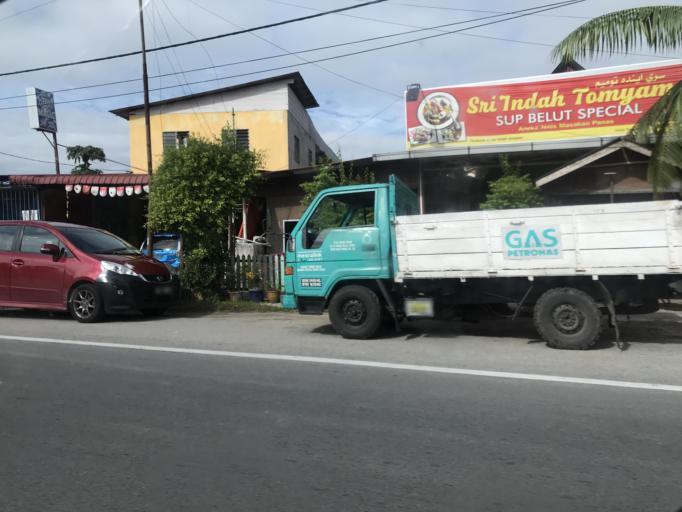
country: MY
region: Kelantan
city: Kota Bharu
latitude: 6.1273
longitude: 102.1803
